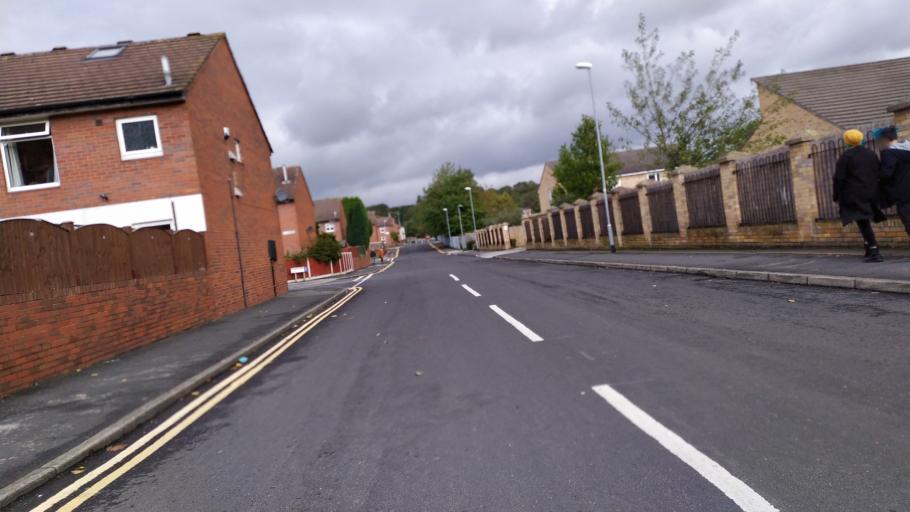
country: GB
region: England
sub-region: City and Borough of Leeds
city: Leeds
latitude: 53.8124
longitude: -1.5492
